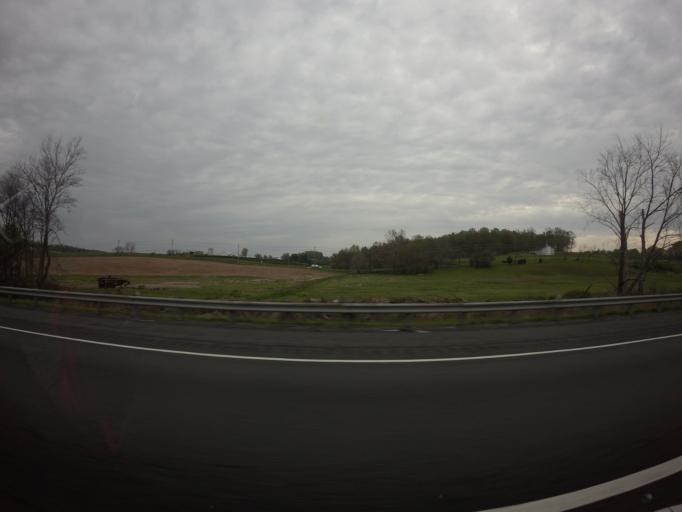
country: US
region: Maryland
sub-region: Carroll County
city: Mount Airy
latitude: 39.3697
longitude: -77.2148
